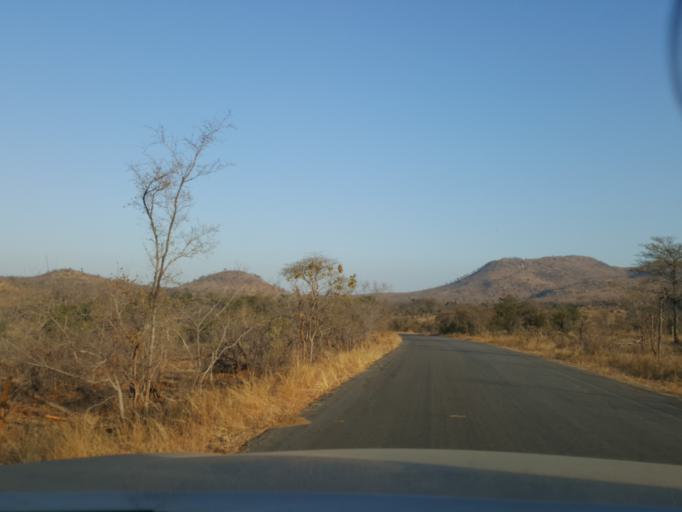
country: SZ
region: Hhohho
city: Ntfonjeni
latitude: -25.4393
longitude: 31.4446
